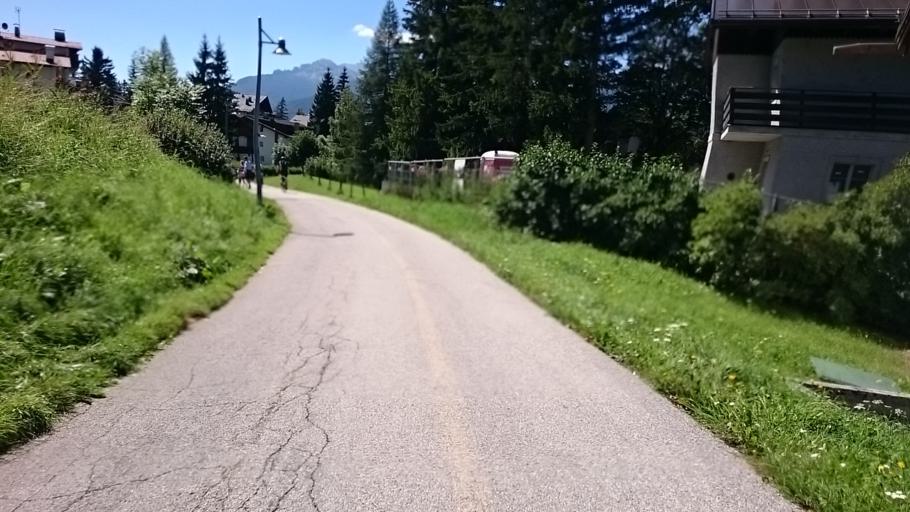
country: IT
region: Veneto
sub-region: Provincia di Belluno
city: Cortina d'Ampezzo
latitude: 46.5429
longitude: 12.1367
